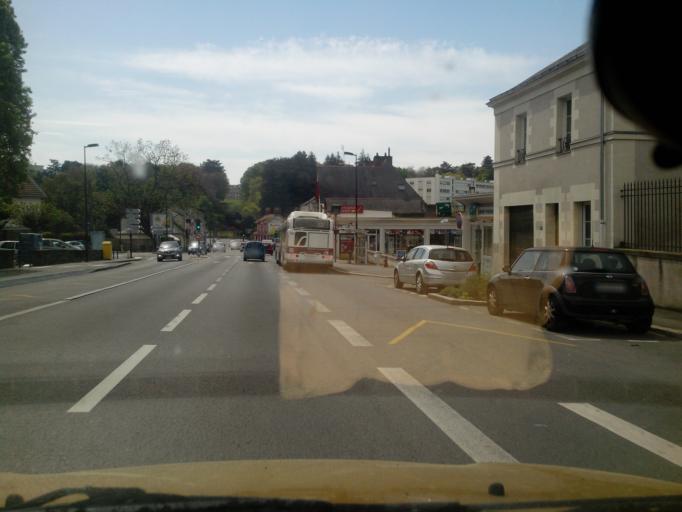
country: FR
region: Pays de la Loire
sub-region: Departement de la Loire-Atlantique
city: Nantes
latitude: 47.2490
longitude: -1.5771
